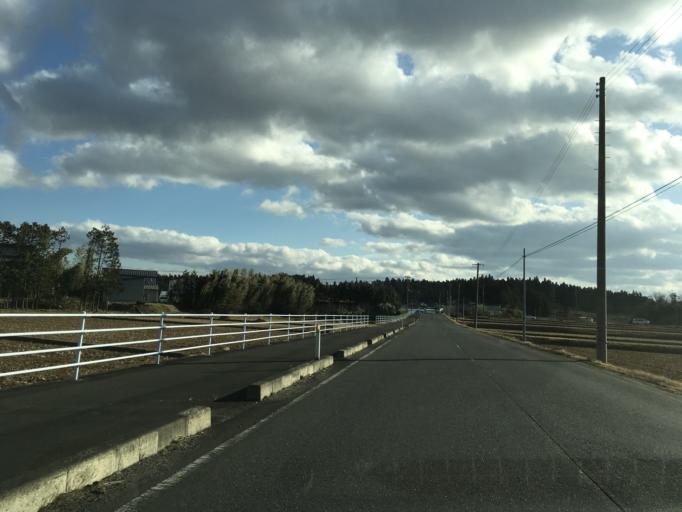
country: JP
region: Iwate
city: Ichinoseki
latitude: 38.8236
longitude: 141.0015
